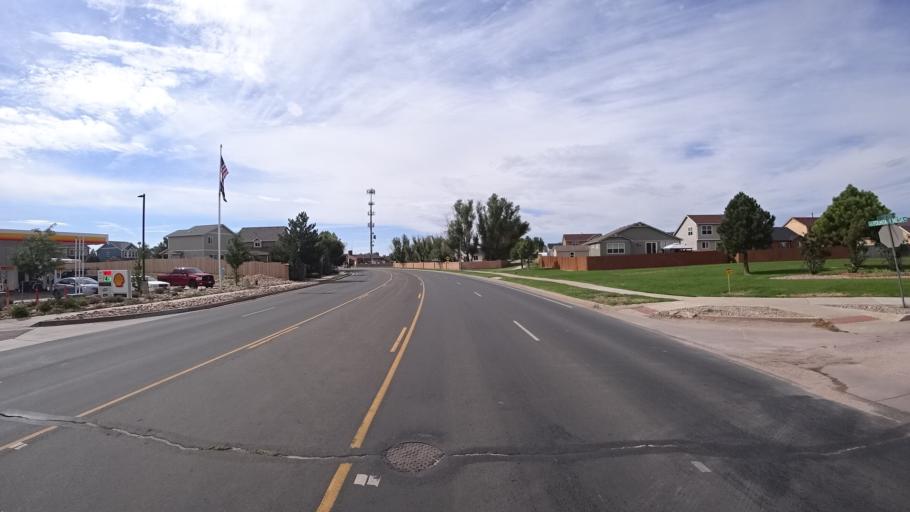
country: US
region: Colorado
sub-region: El Paso County
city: Fountain
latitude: 38.7143
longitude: -104.7014
